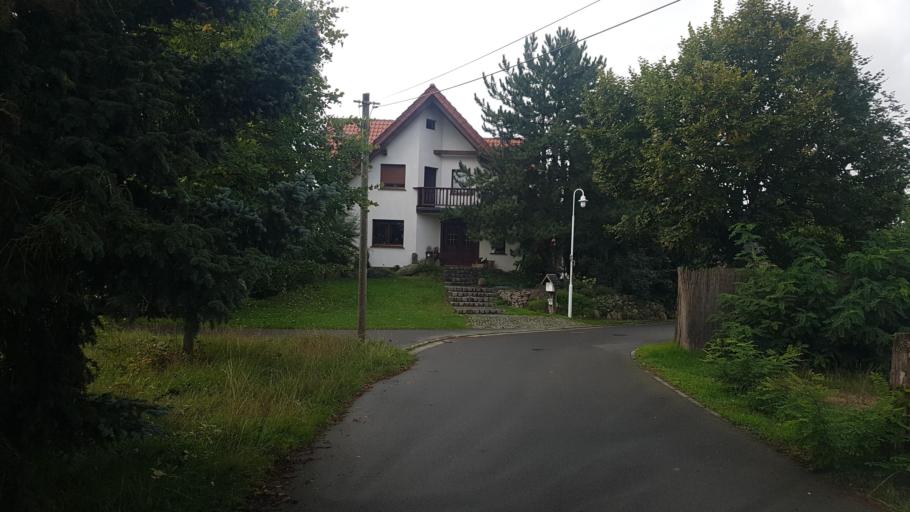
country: DE
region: Brandenburg
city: Elsterwerda
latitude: 51.4772
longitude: 13.4719
